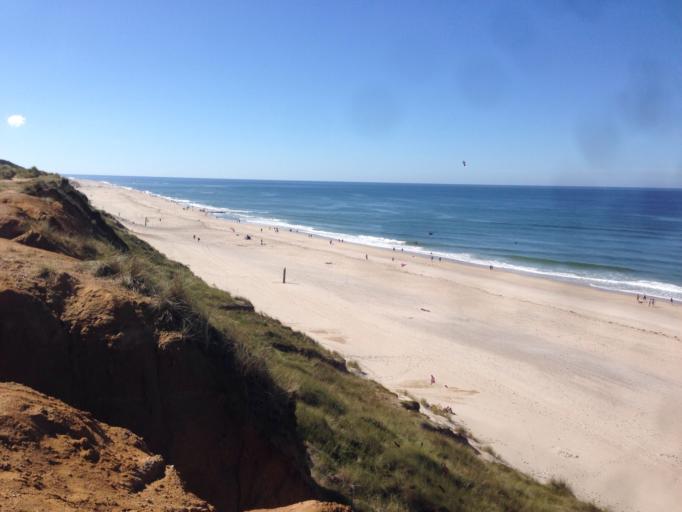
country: DE
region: Schleswig-Holstein
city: Westerland
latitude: 54.9550
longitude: 8.3272
